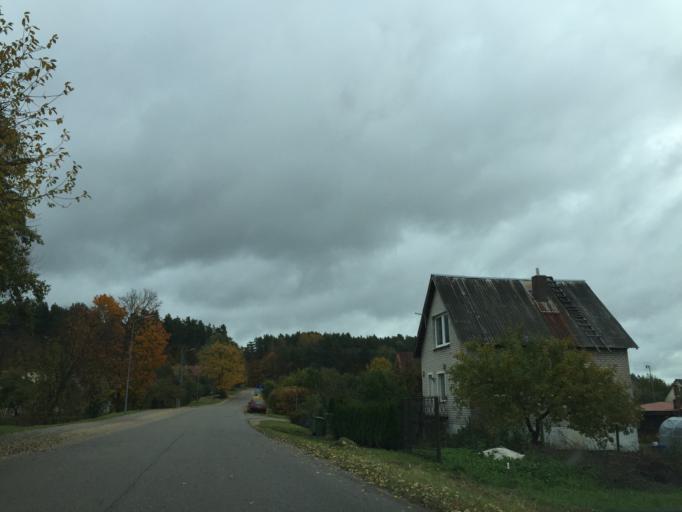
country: LV
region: Ogre
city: Ogre
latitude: 56.7956
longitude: 24.6348
